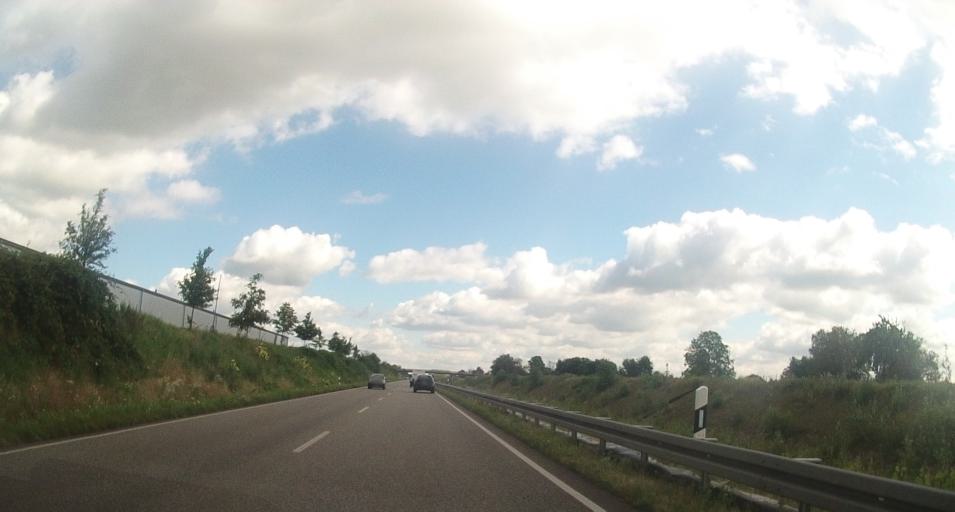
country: DE
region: Baden-Wuerttemberg
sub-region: Karlsruhe Region
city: Bietigheim
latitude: 48.9074
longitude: 8.2630
